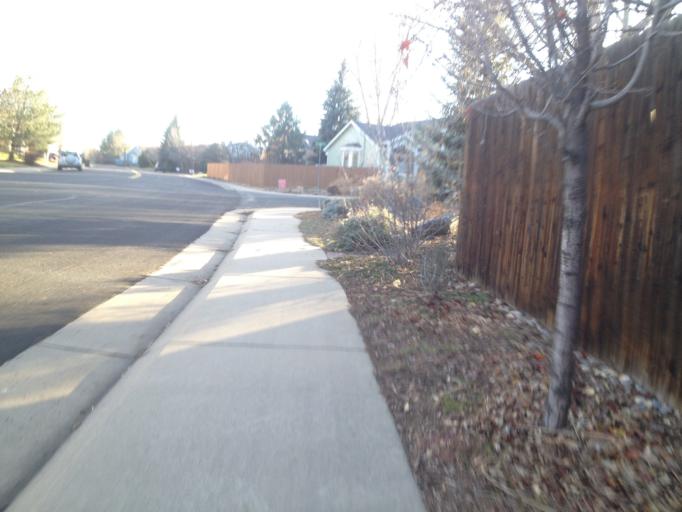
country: US
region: Colorado
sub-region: Boulder County
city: Superior
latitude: 39.9671
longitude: -105.1596
